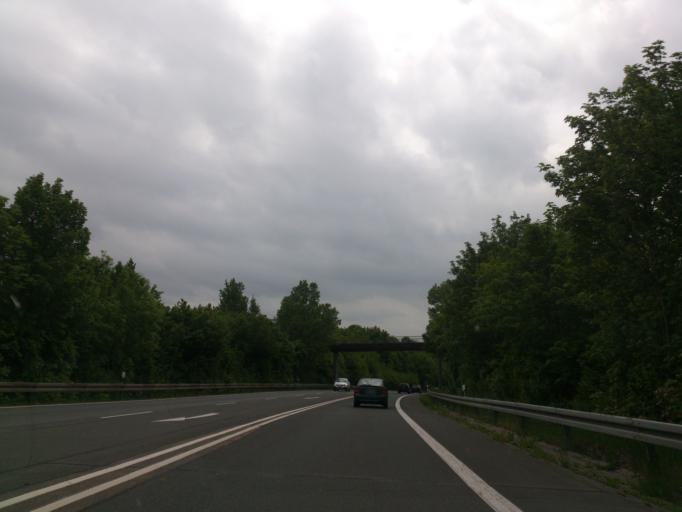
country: DE
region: North Rhine-Westphalia
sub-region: Regierungsbezirk Detmold
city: Willebadessen
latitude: 51.5309
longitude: 9.0189
